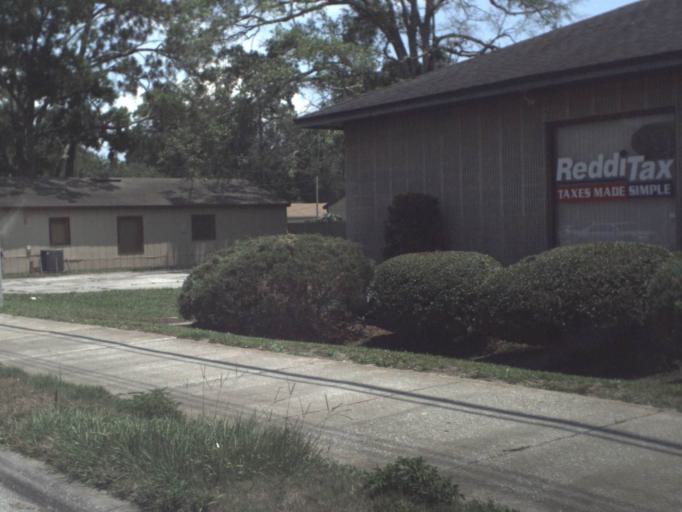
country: US
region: Florida
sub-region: Clay County
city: Bellair-Meadowbrook Terrace
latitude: 30.2481
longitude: -81.7712
